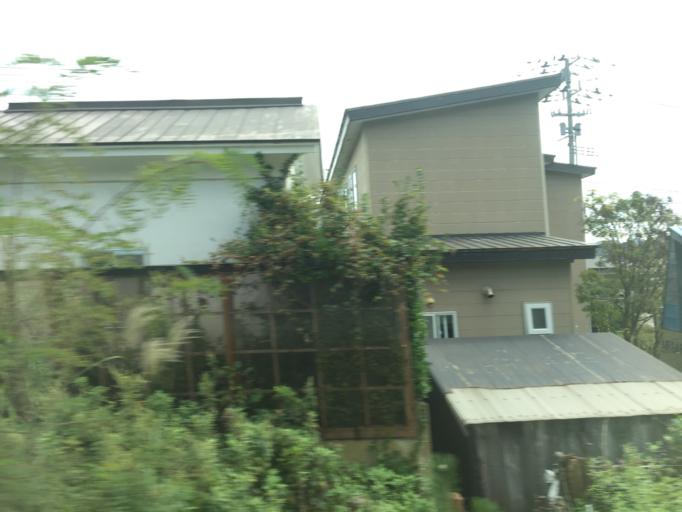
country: JP
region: Aomori
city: Shimokizukuri
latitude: 40.7624
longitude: 140.1631
